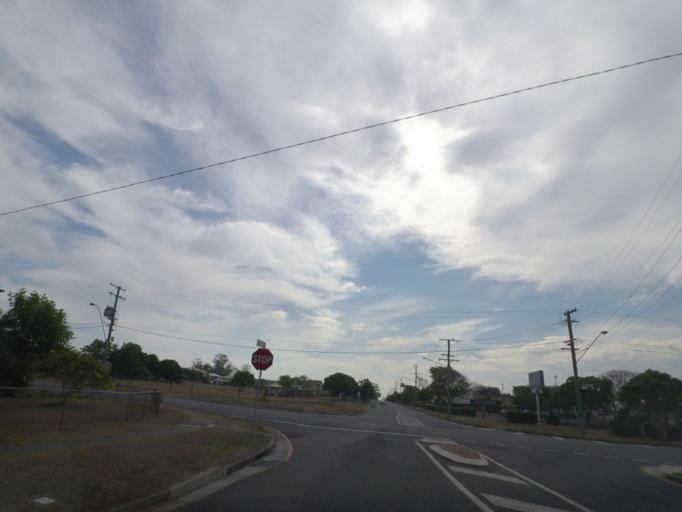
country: AU
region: Queensland
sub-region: Brisbane
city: Richlands
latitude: -27.5919
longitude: 152.9598
